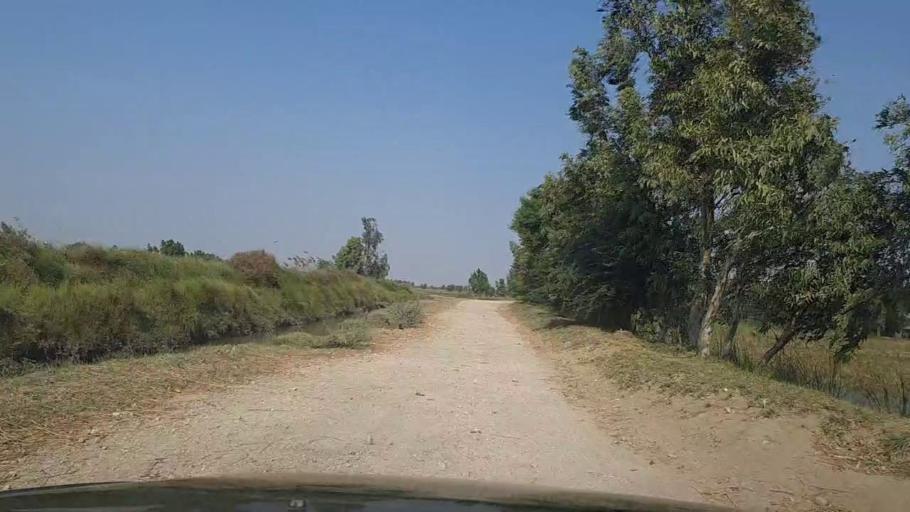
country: PK
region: Sindh
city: Thatta
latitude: 24.6223
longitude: 67.8144
